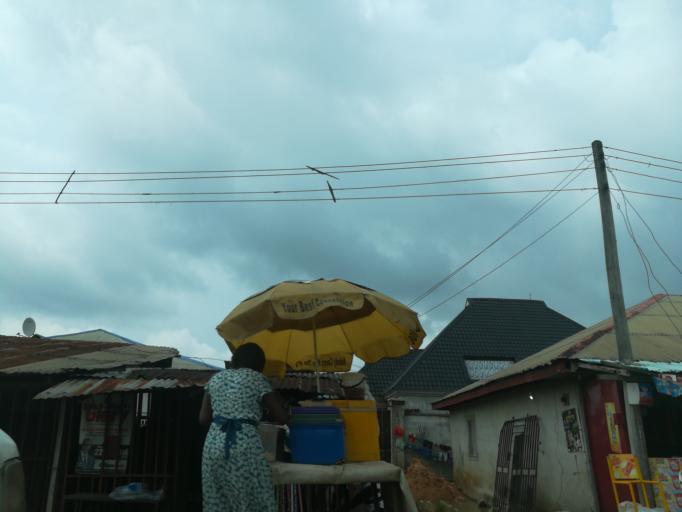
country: NG
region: Rivers
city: Emuoha
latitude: 4.9086
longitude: 6.9859
